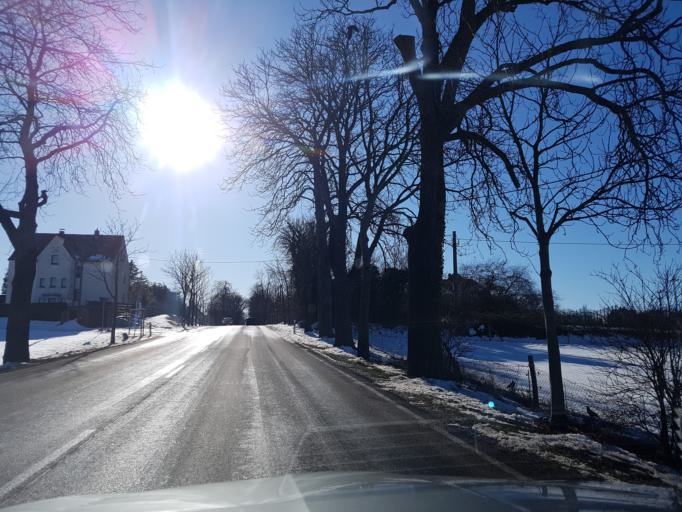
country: DE
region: Saxony
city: Moritzburg
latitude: 51.1298
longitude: 13.6858
